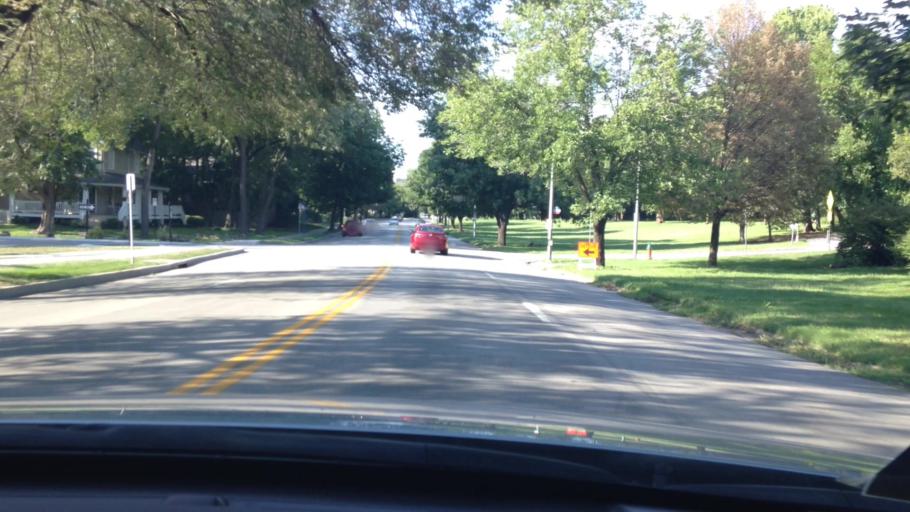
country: US
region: Kansas
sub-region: Johnson County
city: Mission Hills
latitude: 39.0287
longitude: -94.5844
